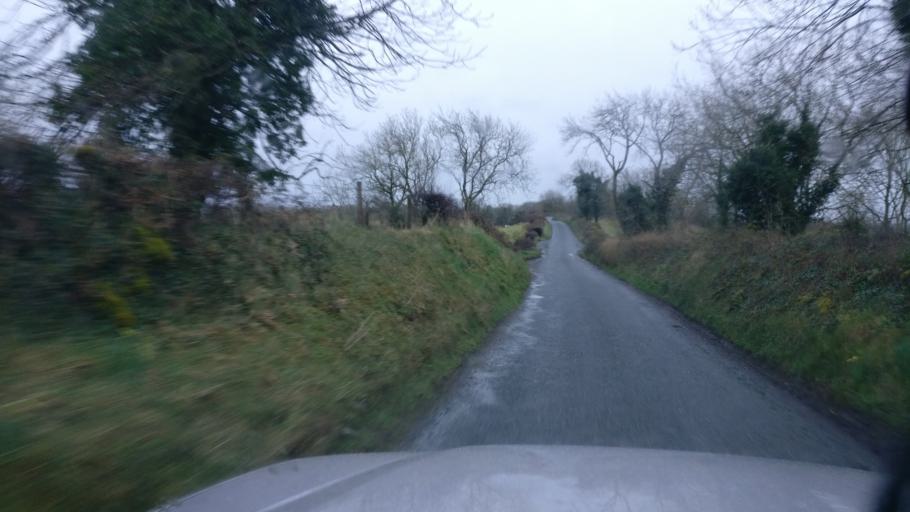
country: IE
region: Connaught
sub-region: County Galway
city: Ballinasloe
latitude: 53.3021
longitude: -8.2757
